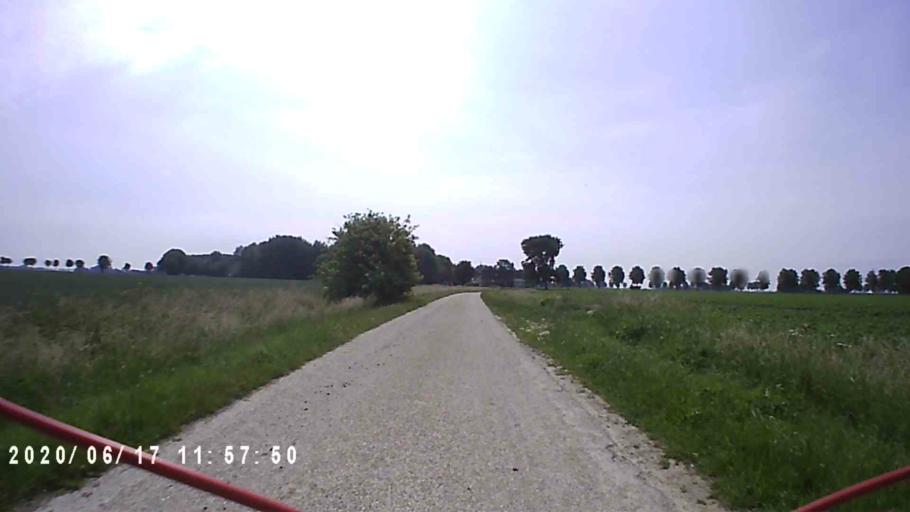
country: NL
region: Groningen
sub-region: Gemeente De Marne
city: Ulrum
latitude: 53.3457
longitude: 6.3261
